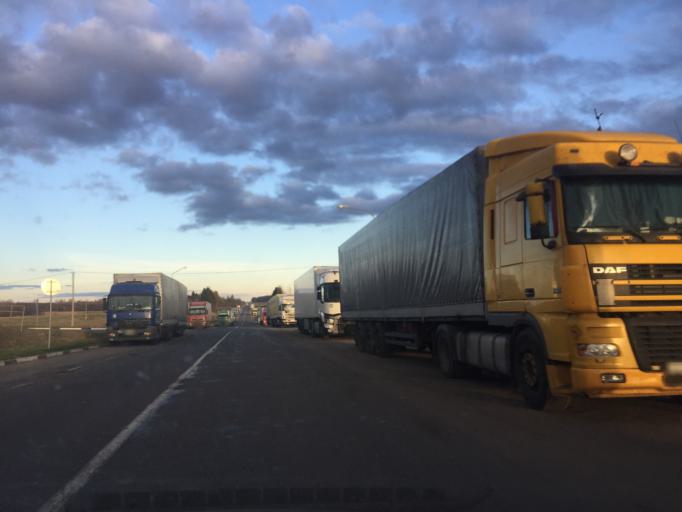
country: BY
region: Vitebsk
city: Myory
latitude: 55.8160
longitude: 27.6727
